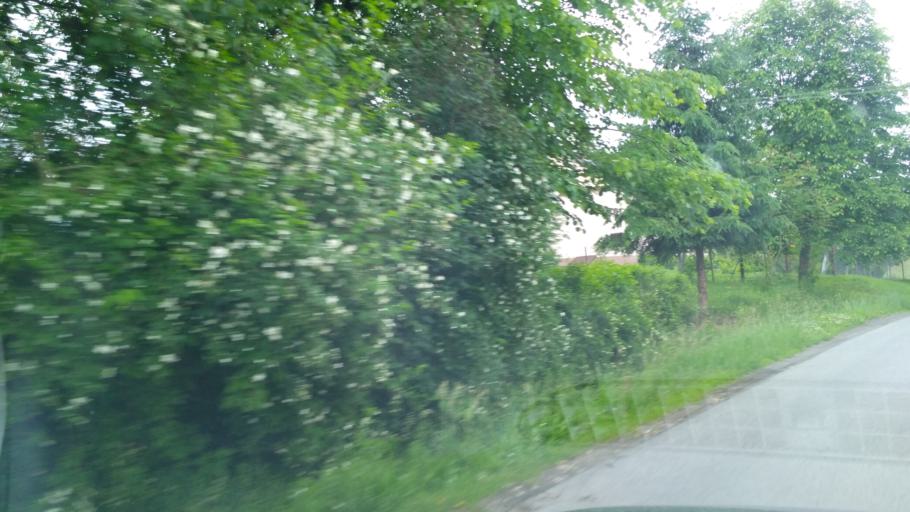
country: PL
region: Subcarpathian Voivodeship
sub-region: Powiat przemyski
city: Nienadowa
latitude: 49.8461
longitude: 22.4129
